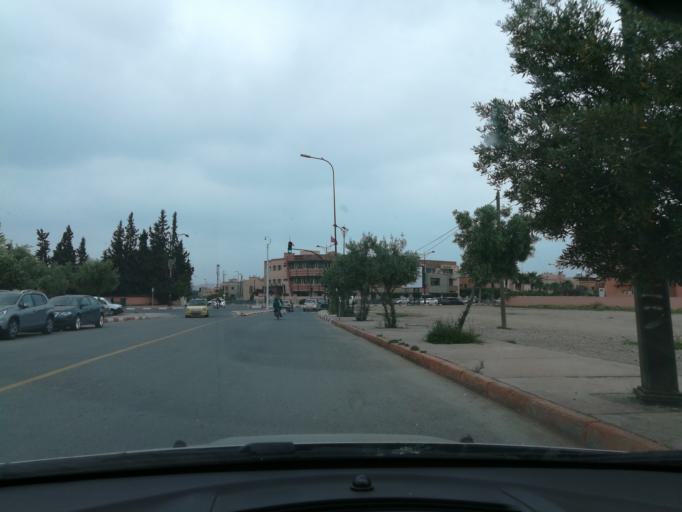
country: MA
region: Marrakech-Tensift-Al Haouz
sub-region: Marrakech
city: Marrakesh
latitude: 31.6773
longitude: -7.9998
